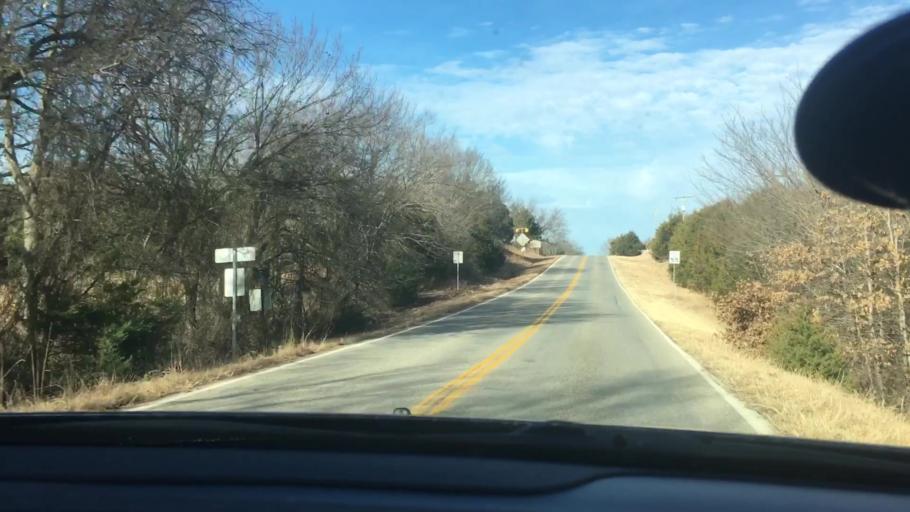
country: US
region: Oklahoma
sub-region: Seminole County
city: Konawa
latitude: 34.9612
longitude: -96.7620
